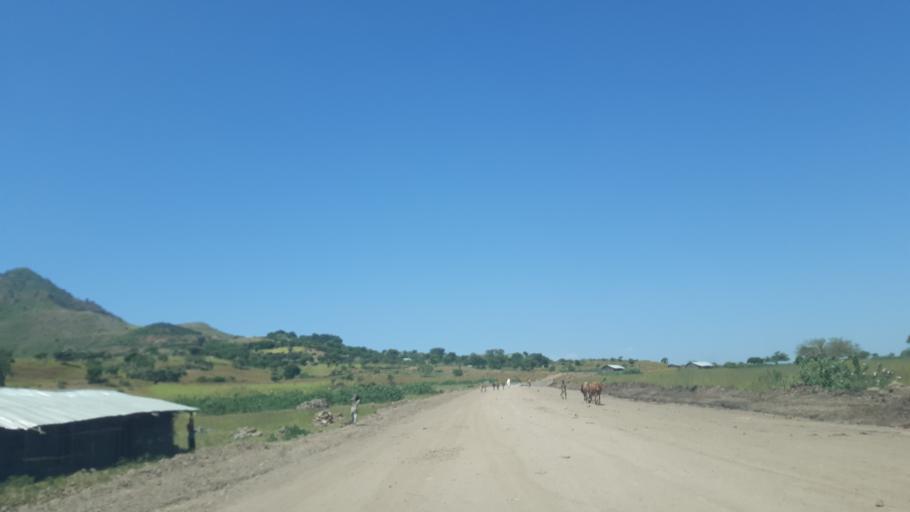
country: ET
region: Amhara
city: Dabat
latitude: 13.1585
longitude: 37.6096
